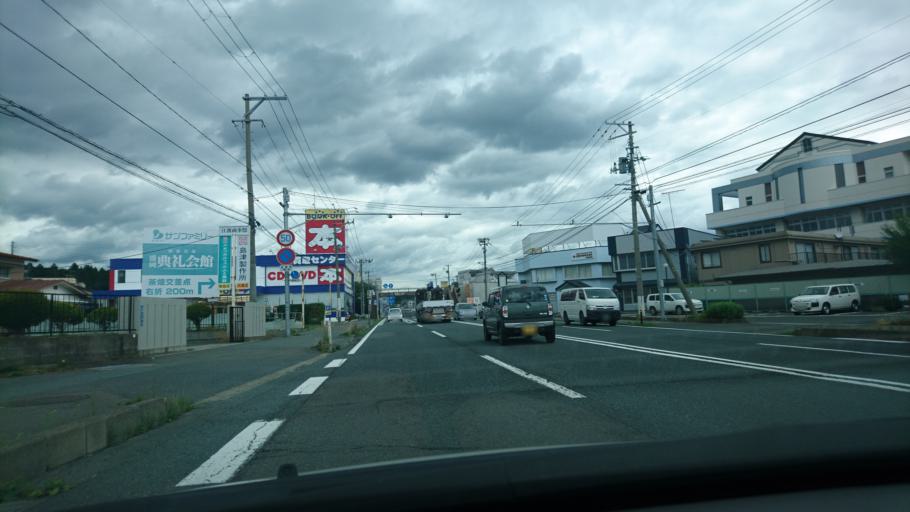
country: JP
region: Iwate
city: Morioka-shi
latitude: 39.6905
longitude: 141.1656
